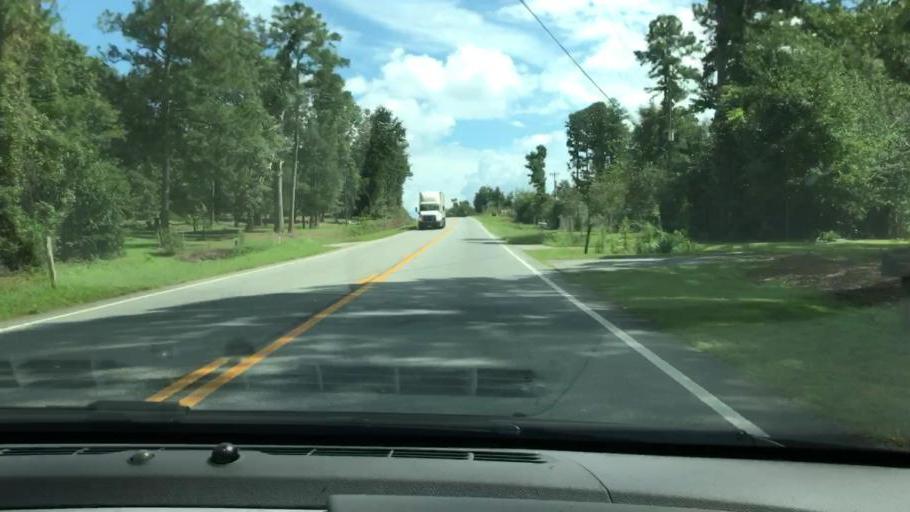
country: US
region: Georgia
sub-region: Quitman County
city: Georgetown
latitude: 31.8640
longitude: -85.0720
